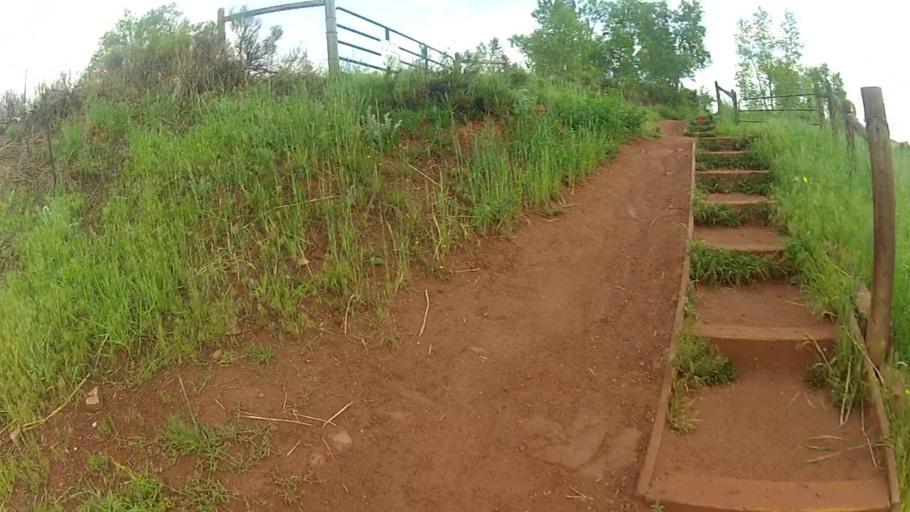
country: US
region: Colorado
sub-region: Larimer County
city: Loveland
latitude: 40.4129
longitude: -105.1529
